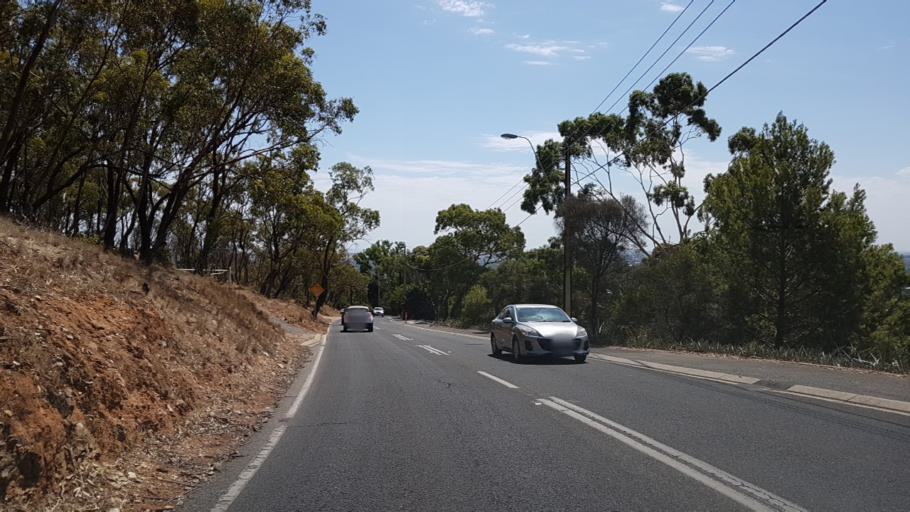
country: AU
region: South Australia
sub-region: Mitcham
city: Mitcham
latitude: -34.9866
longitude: 138.6241
